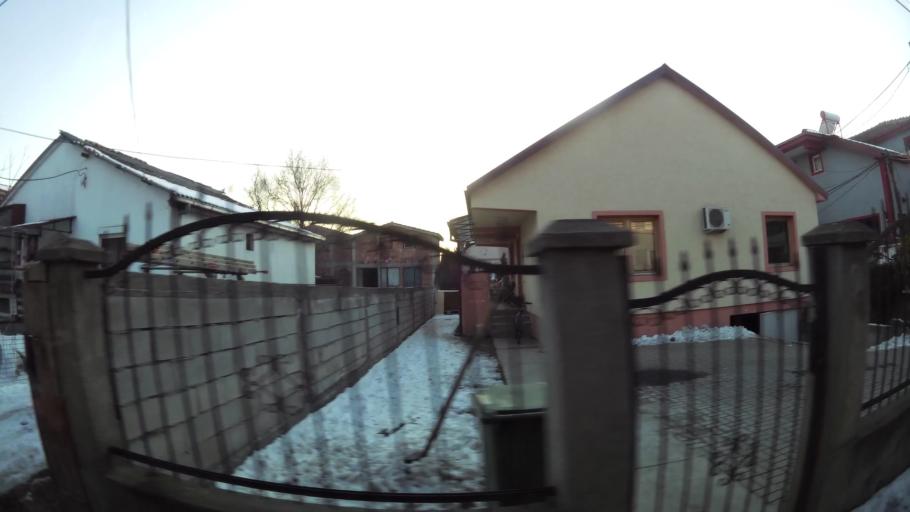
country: MK
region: Kisela Voda
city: Kisela Voda
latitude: 41.9800
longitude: 21.4903
